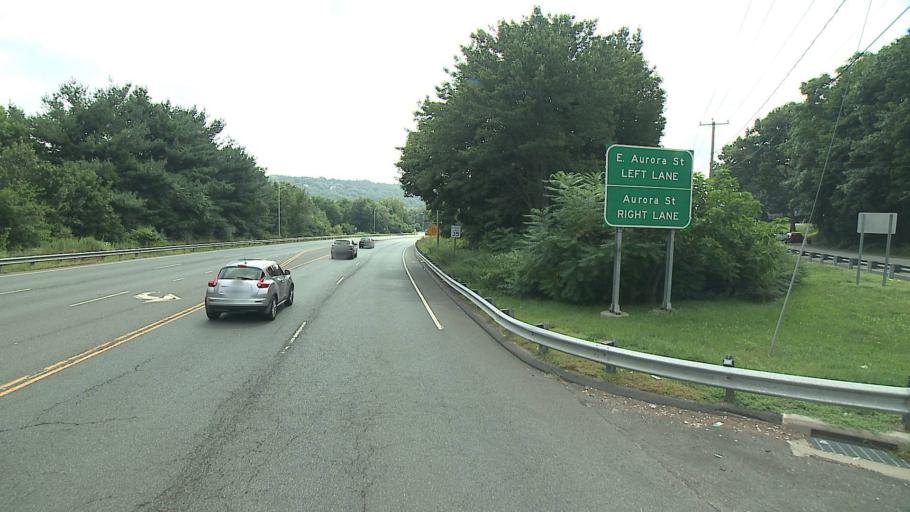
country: US
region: Connecticut
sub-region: New Haven County
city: Waterbury
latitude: 41.5727
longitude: -73.0623
